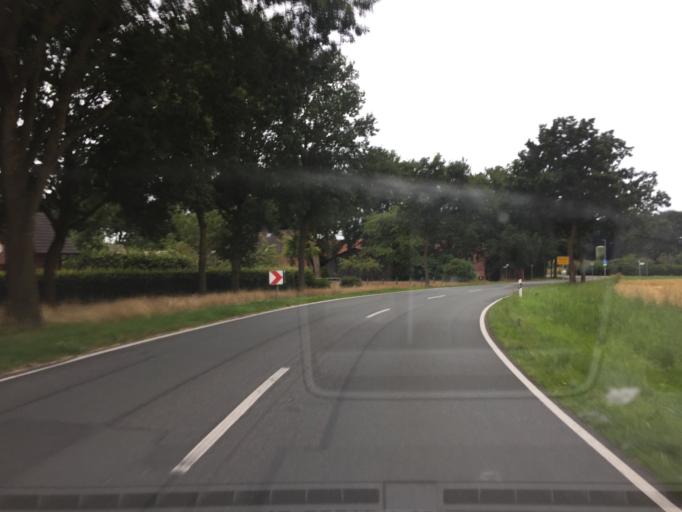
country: DE
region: Lower Saxony
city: Ehrenburg
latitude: 52.7536
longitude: 8.7177
